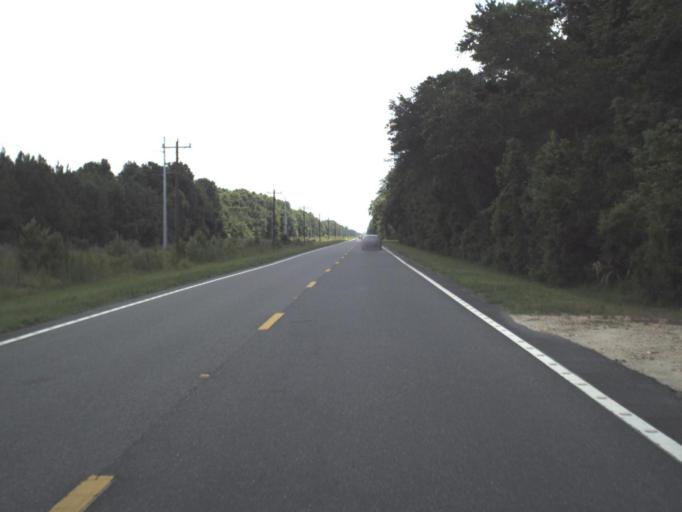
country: US
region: Florida
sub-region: Levy County
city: Chiefland
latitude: 29.2732
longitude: -82.8650
